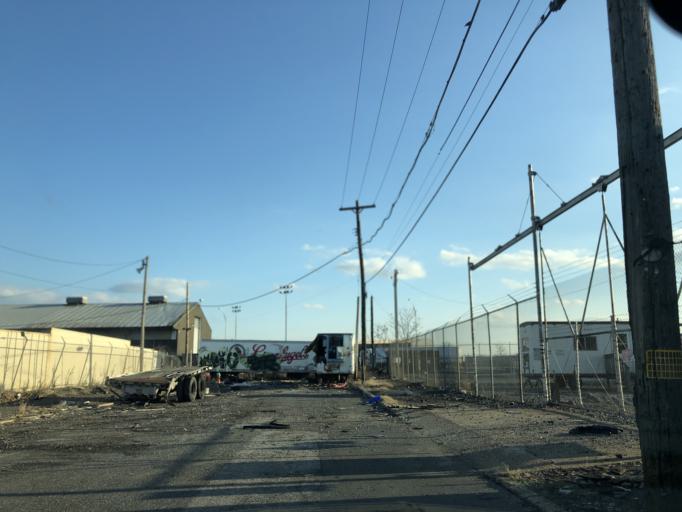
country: US
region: New Jersey
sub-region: Camden County
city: Merchantville
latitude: 39.9804
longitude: -75.0923
